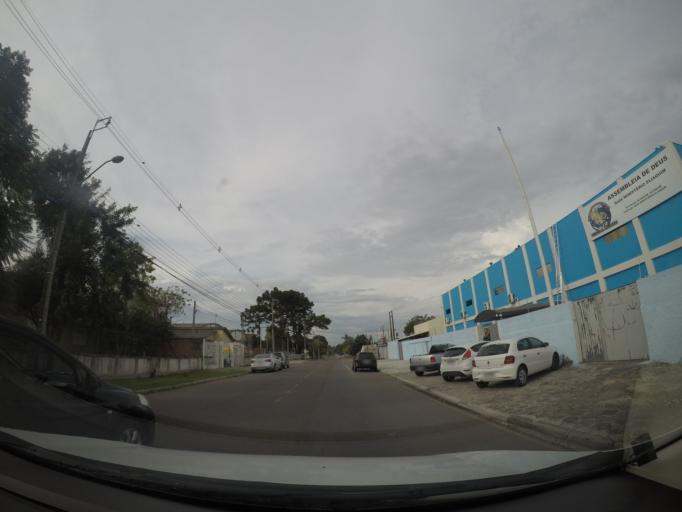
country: BR
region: Parana
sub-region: Sao Jose Dos Pinhais
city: Sao Jose dos Pinhais
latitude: -25.4967
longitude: -49.2372
